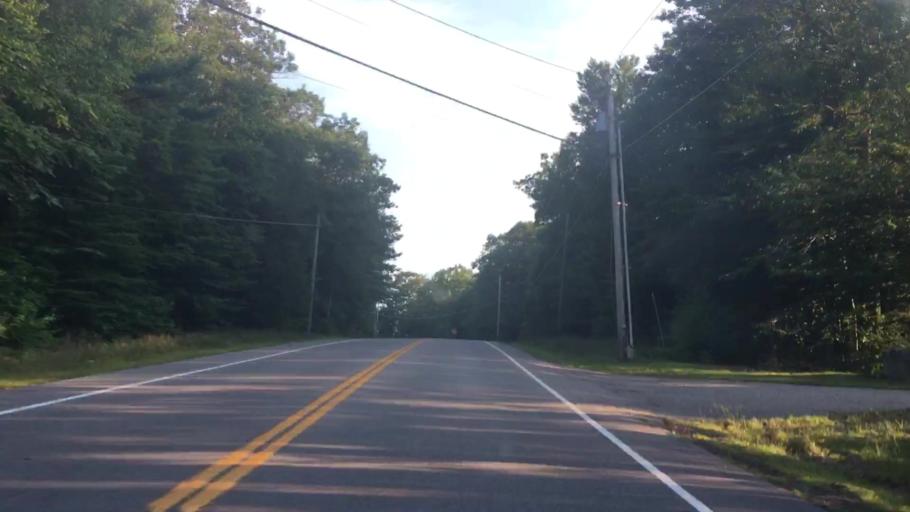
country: US
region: New Hampshire
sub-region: Belknap County
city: Gilmanton
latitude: 43.4418
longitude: -71.4190
